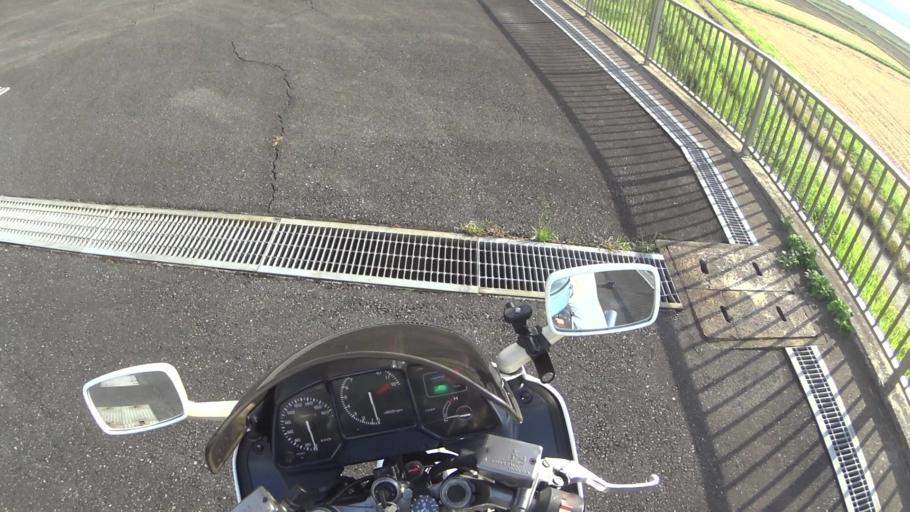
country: JP
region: Kyoto
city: Miyazu
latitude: 35.5735
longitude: 135.1707
